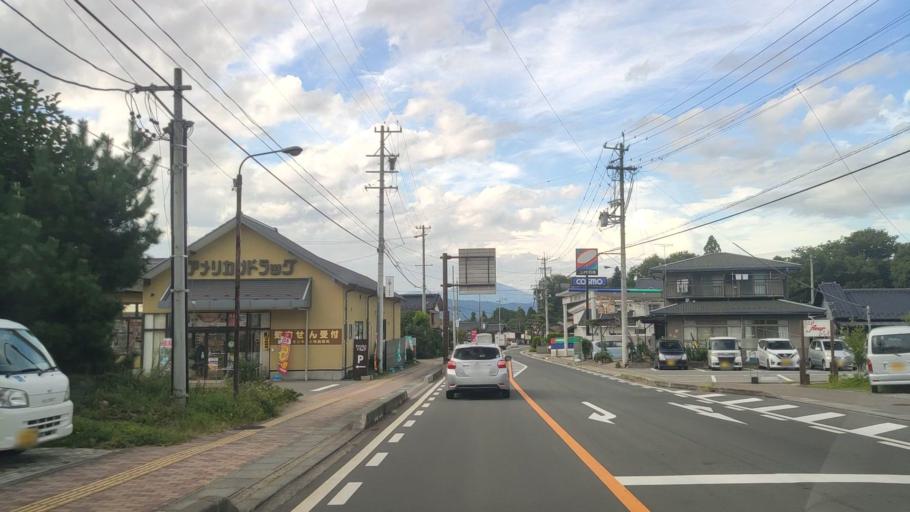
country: JP
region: Nagano
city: Suzaka
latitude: 36.6905
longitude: 138.3154
